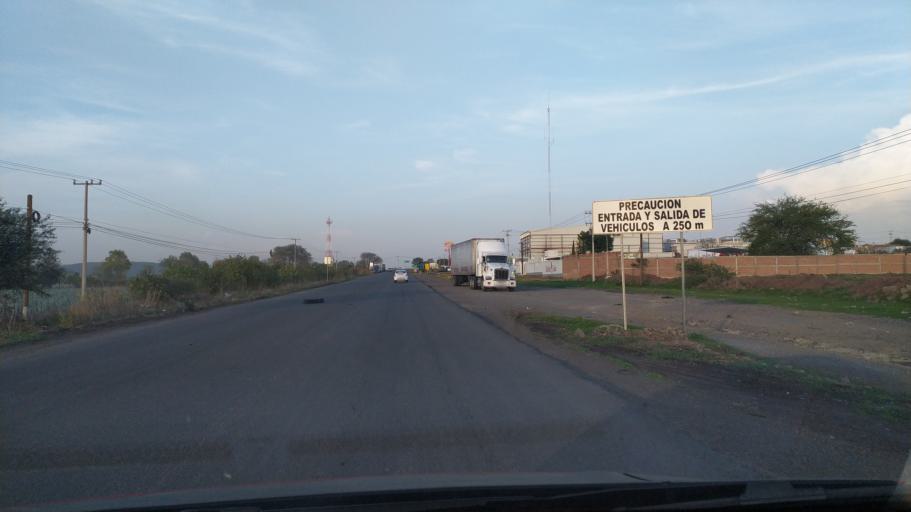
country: MX
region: Michoacan
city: Vistahermosa de Negrete
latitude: 20.2678
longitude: -102.4526
